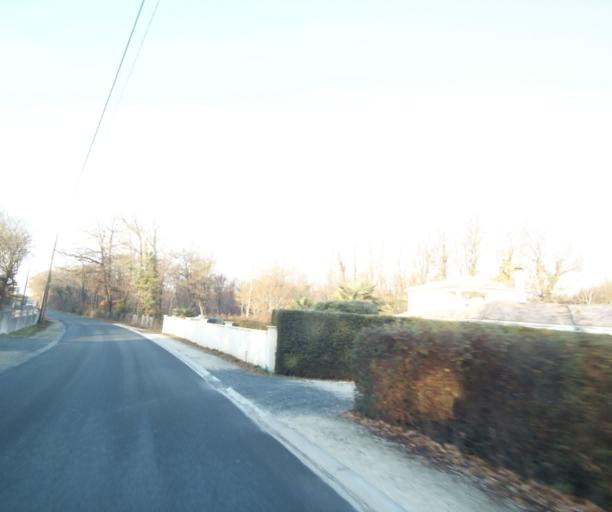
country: FR
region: Poitou-Charentes
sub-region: Departement de la Charente-Maritime
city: Fontcouverte
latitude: 45.7637
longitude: -0.5896
